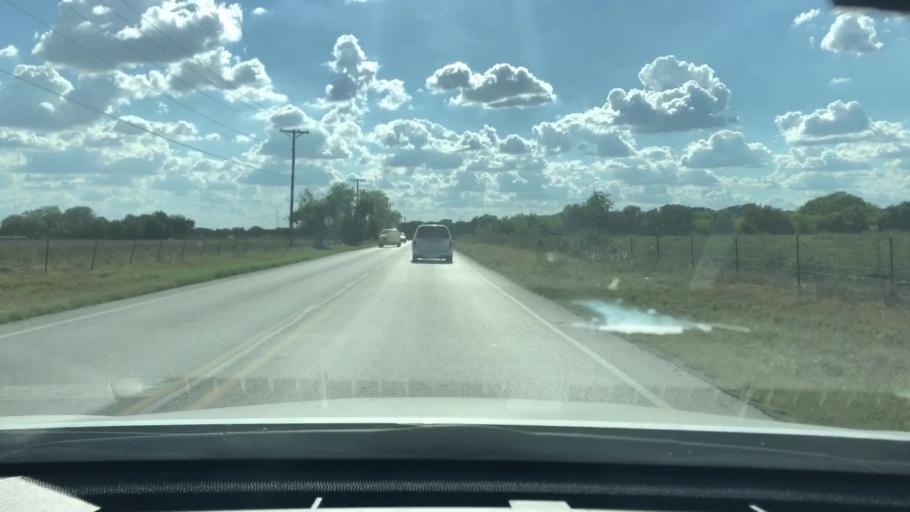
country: US
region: Texas
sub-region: Guadalupe County
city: Northcliff
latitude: 29.6568
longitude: -98.2048
